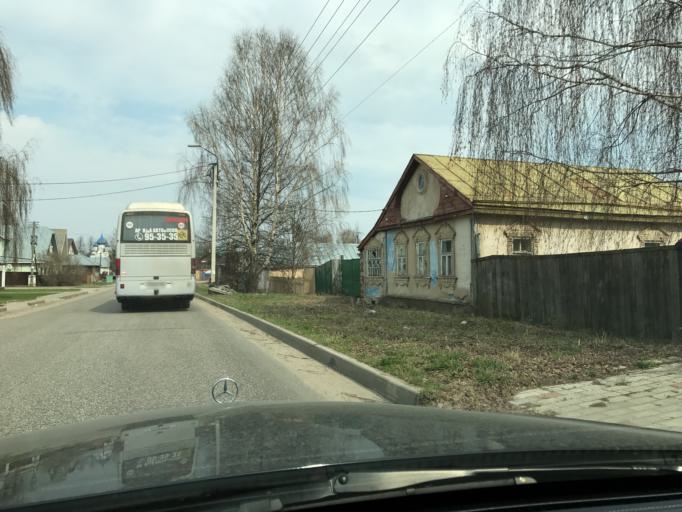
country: RU
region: Vladimir
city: Suzdal'
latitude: 56.4124
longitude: 40.4333
